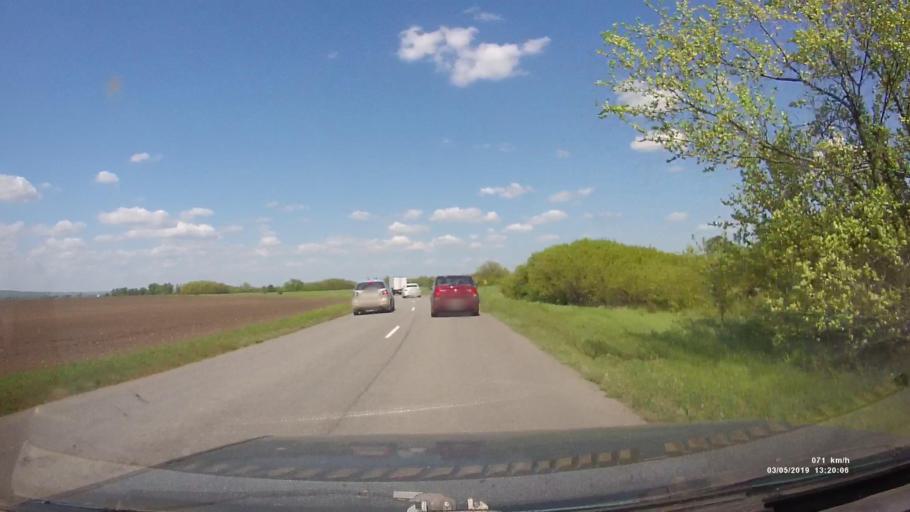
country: RU
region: Rostov
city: Semikarakorsk
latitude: 47.5450
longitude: 40.7541
